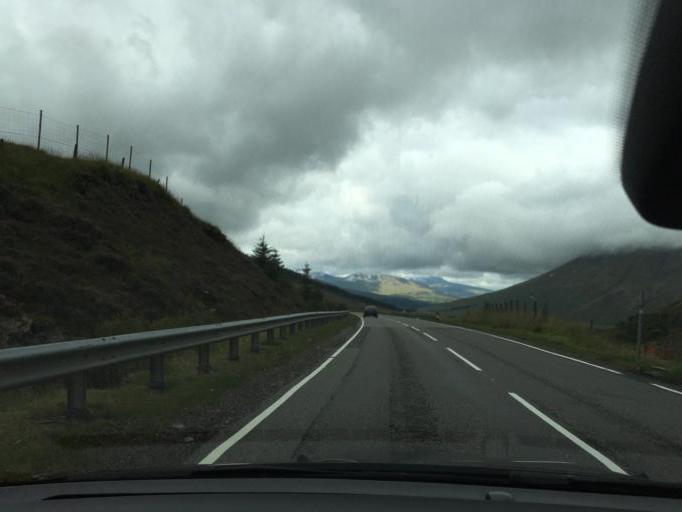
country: GB
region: Scotland
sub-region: Argyll and Bute
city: Garelochhead
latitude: 56.4606
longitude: -4.7146
